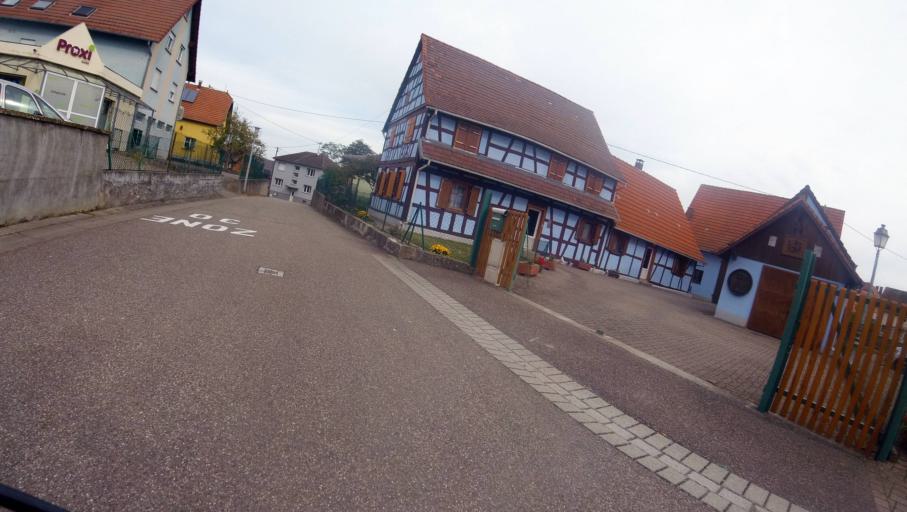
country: DE
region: Rheinland-Pfalz
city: Scheibenhardt
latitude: 48.9314
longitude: 8.1536
